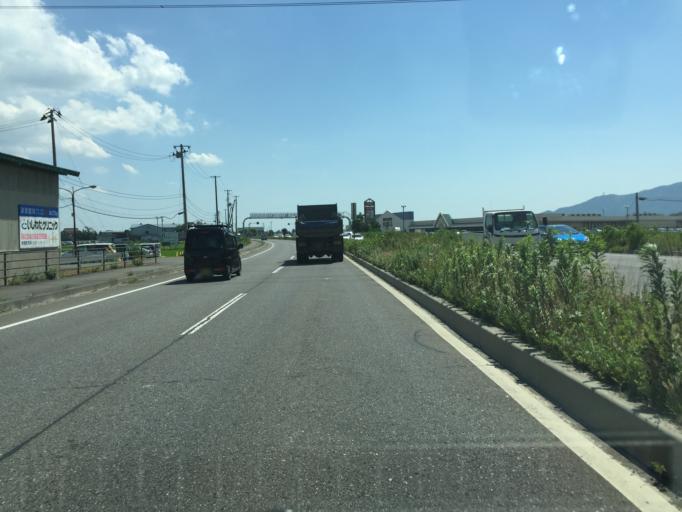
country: JP
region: Fukushima
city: Motomiya
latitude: 37.5447
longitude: 140.3979
